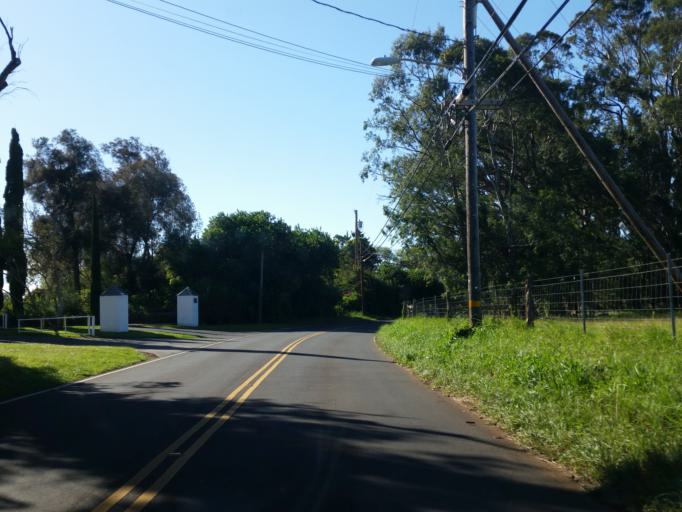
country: US
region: Hawaii
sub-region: Maui County
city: Makawao
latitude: 20.8408
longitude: -156.3085
